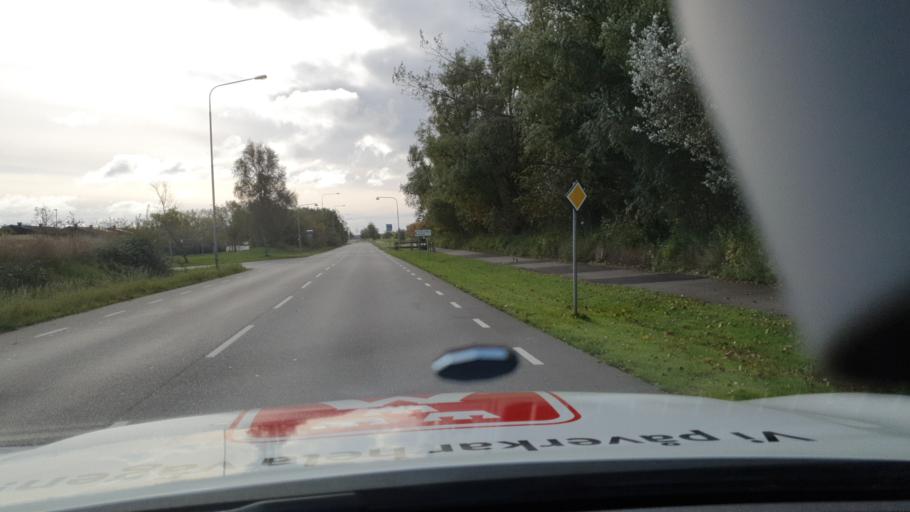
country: SE
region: Skane
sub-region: Vellinge Kommun
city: Vellinge
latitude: 55.4632
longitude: 13.0191
